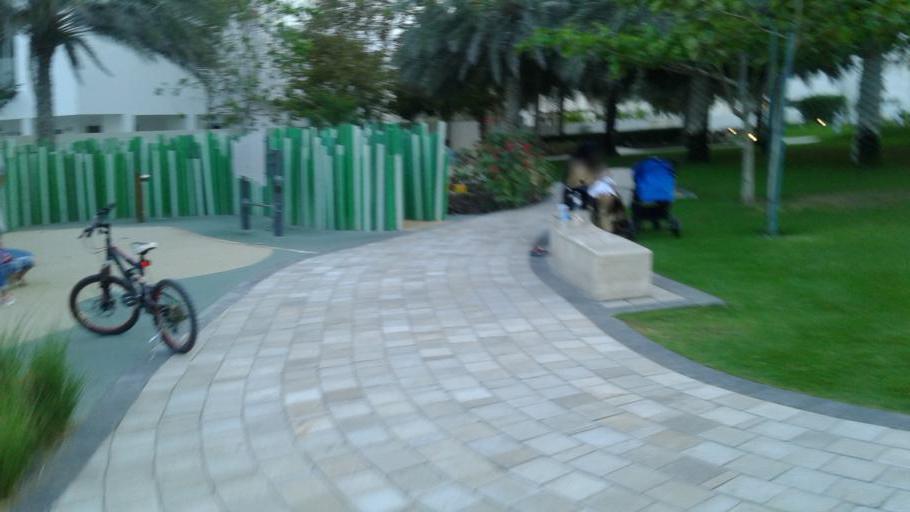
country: OM
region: Muhafazat Masqat
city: As Sib al Jadidah
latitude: 23.6254
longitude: 58.2747
